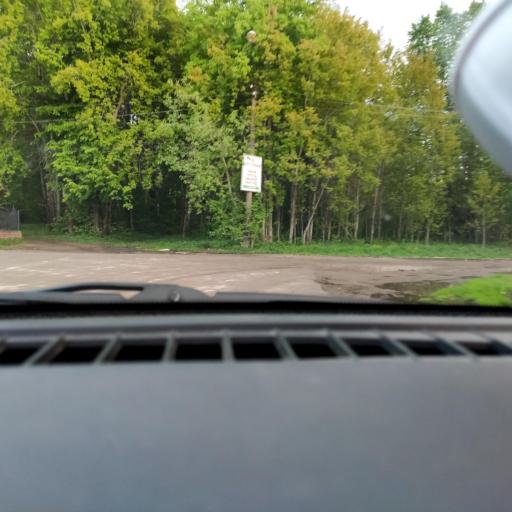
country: RU
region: Perm
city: Perm
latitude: 58.0871
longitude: 56.3839
